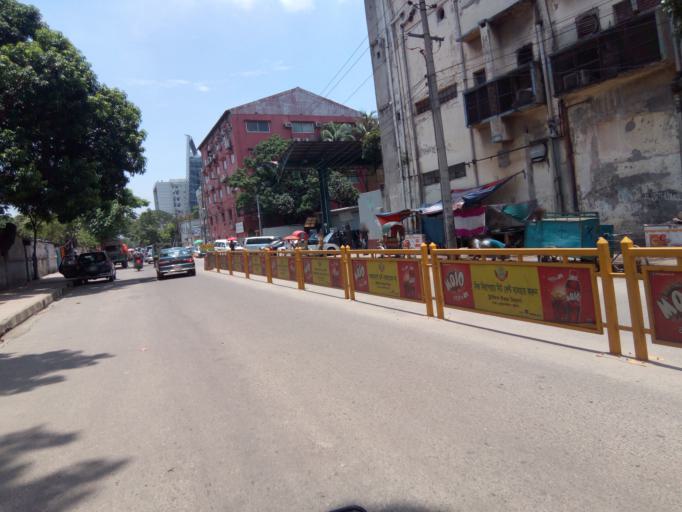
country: BD
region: Dhaka
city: Paltan
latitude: 23.7636
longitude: 90.4005
